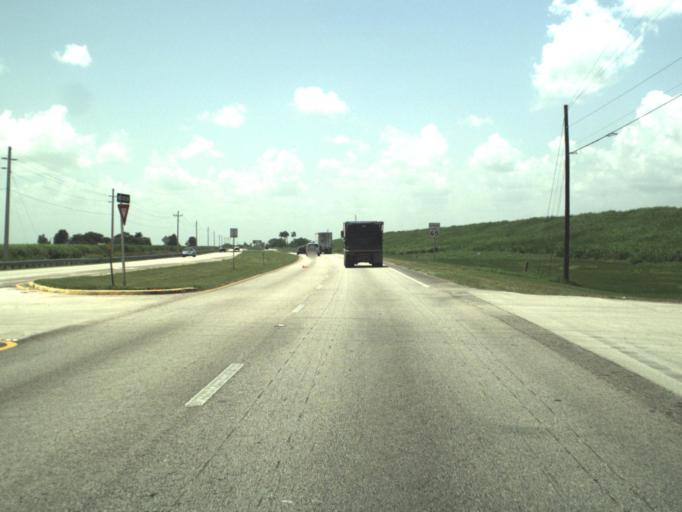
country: US
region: Florida
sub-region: Palm Beach County
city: South Bay
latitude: 26.6801
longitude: -80.7320
